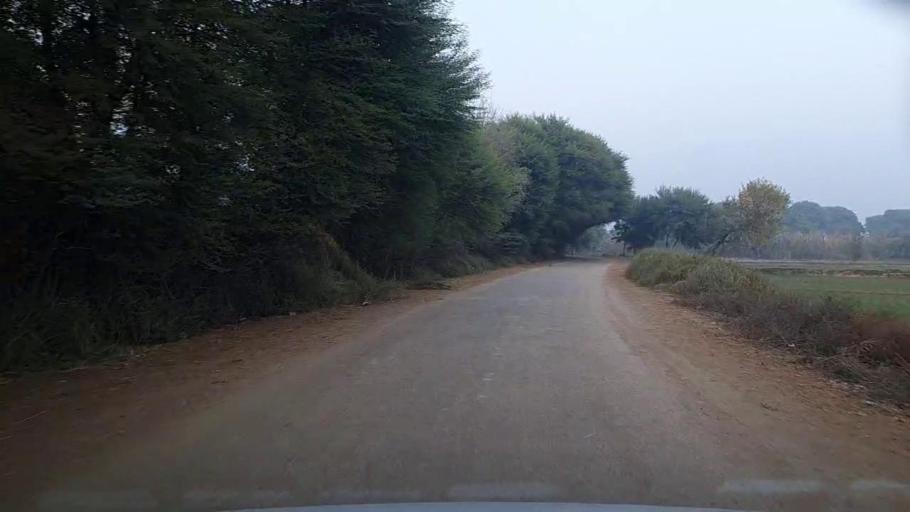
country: PK
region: Sindh
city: Bozdar
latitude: 27.0611
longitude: 68.5948
